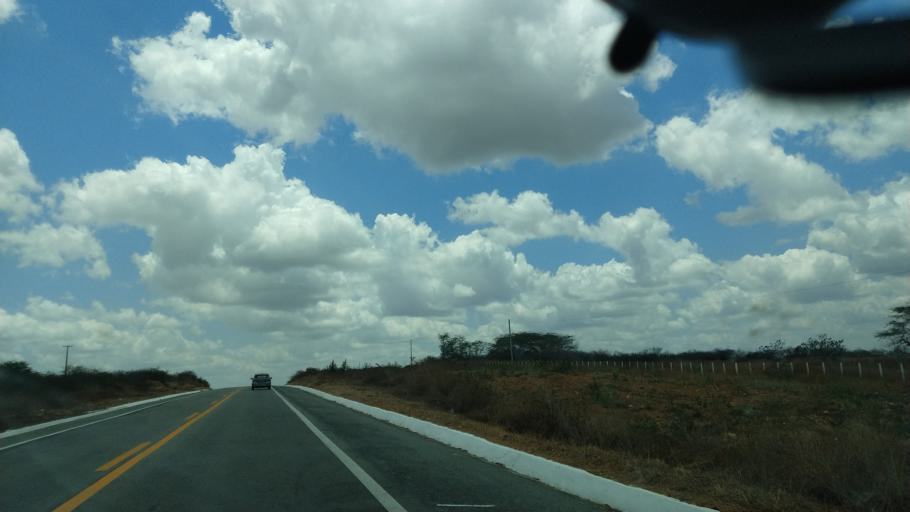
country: BR
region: Rio Grande do Norte
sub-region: Cerro Cora
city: Cerro Cora
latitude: -6.1900
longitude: -36.2264
